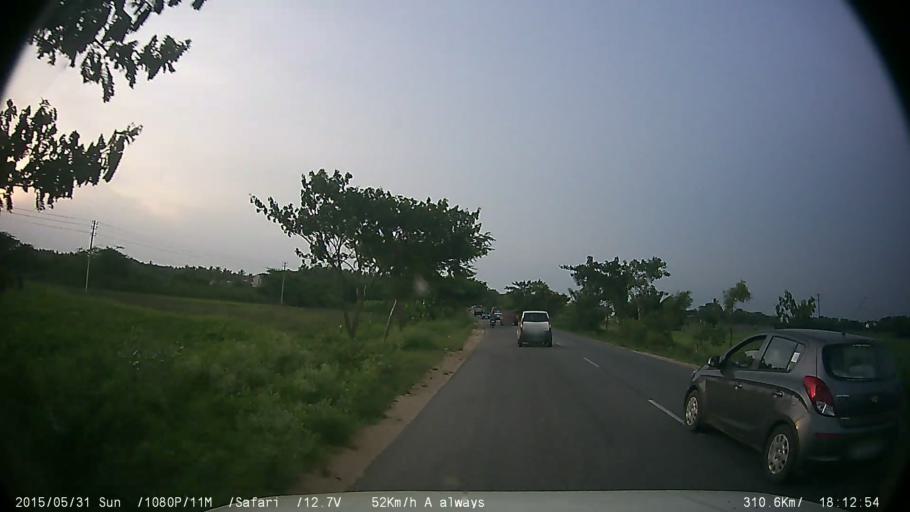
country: IN
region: Karnataka
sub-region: Mysore
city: Nanjangud
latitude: 12.0989
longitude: 76.6720
